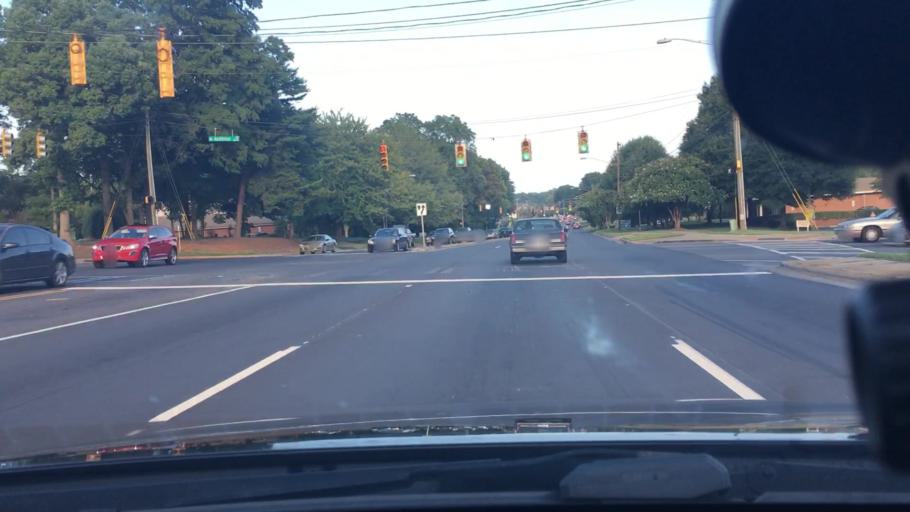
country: US
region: North Carolina
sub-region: Mecklenburg County
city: Matthews
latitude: 35.2039
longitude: -80.7507
